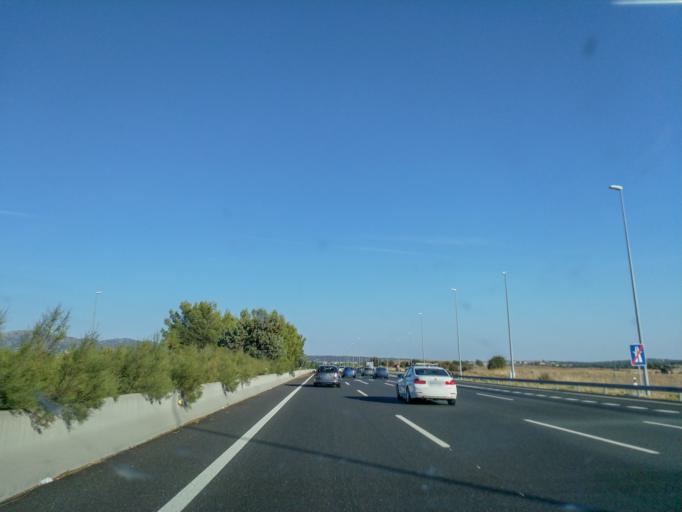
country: ES
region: Madrid
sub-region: Provincia de Madrid
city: Alpedrete
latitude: 40.6457
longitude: -4.0493
